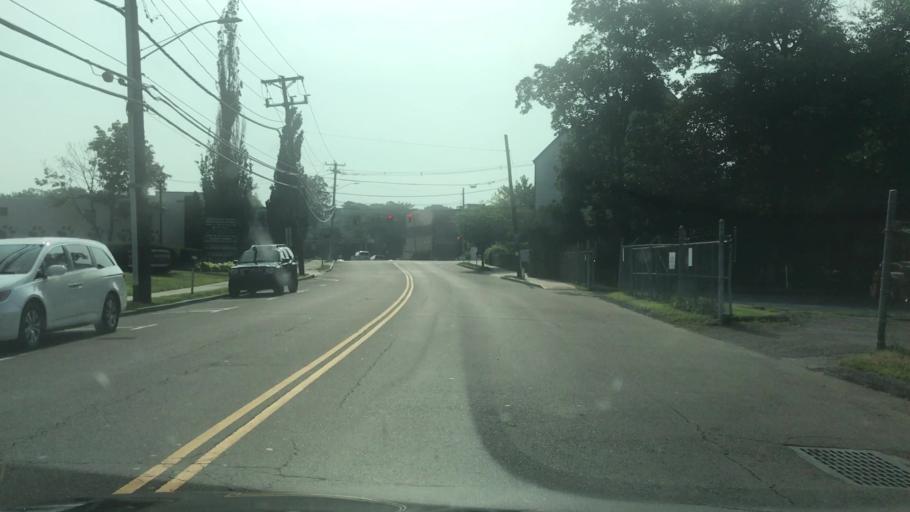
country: US
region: Connecticut
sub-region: Fairfield County
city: Greenwich
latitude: 41.0215
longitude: -73.6303
